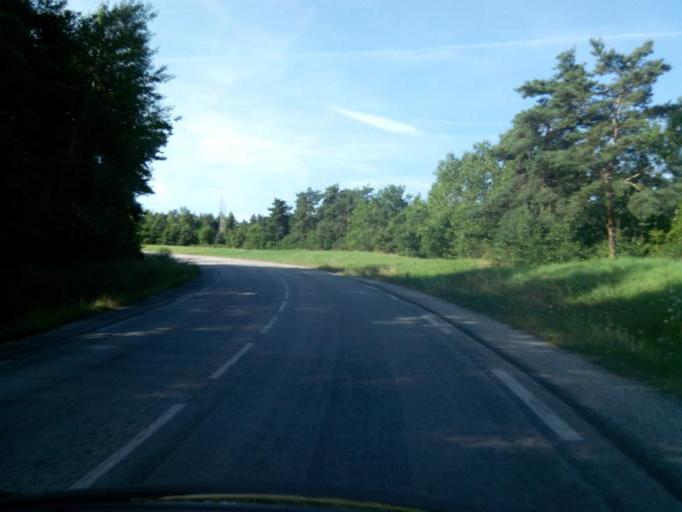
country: FR
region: Auvergne
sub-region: Departement de la Haute-Loire
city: Bas-en-Basset
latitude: 45.2826
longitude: 4.1100
